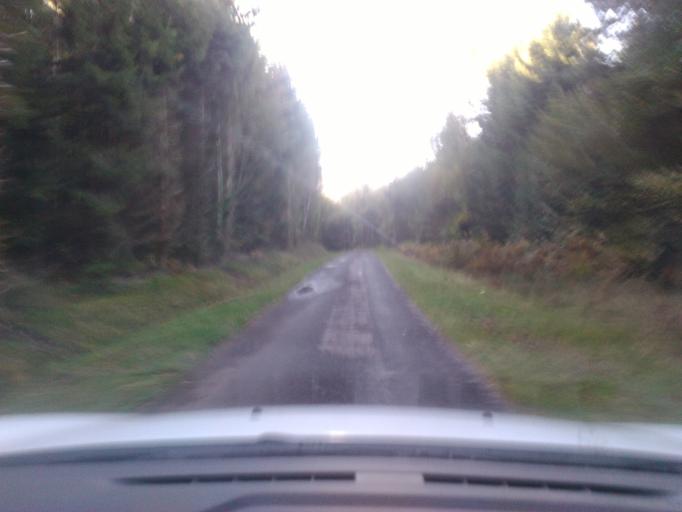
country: FR
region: Lorraine
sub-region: Departement des Vosges
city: Jeanmenil
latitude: 48.2813
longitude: 6.7407
